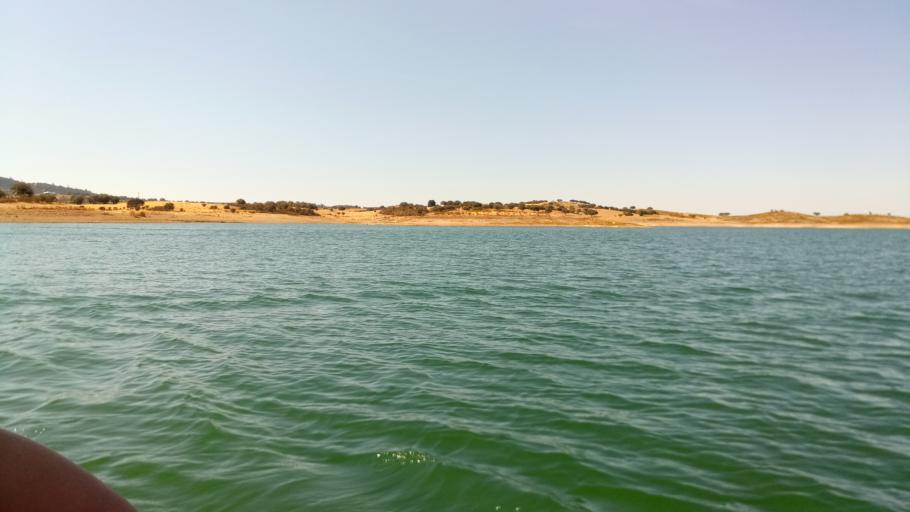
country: PT
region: Evora
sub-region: Mourao
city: Mourao
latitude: 38.4339
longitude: -7.3459
